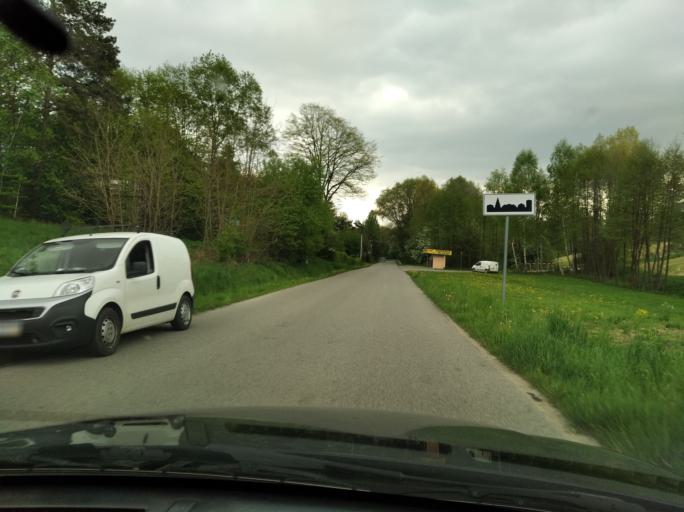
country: PL
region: Subcarpathian Voivodeship
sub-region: Powiat debicki
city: Leki Gorne
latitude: 49.9786
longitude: 21.1592
